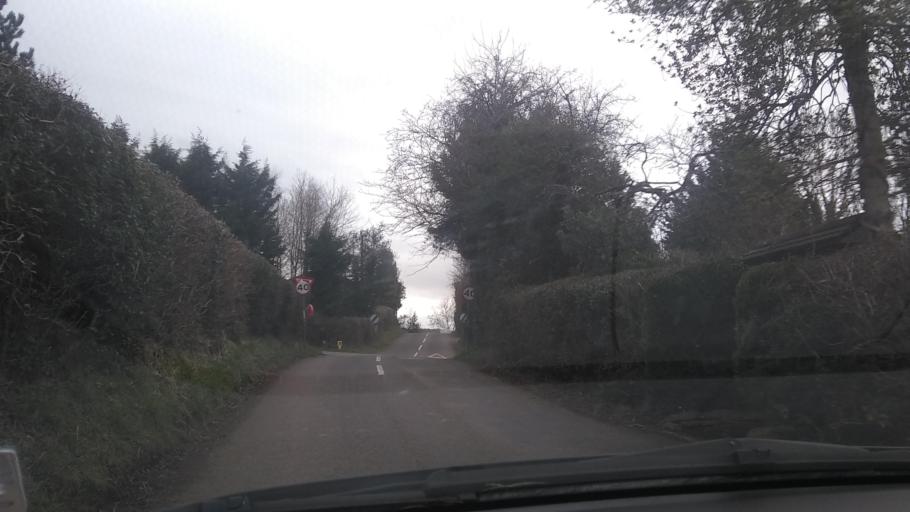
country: GB
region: England
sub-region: Shropshire
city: Cleobury Mortimer
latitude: 52.3718
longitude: -2.4051
